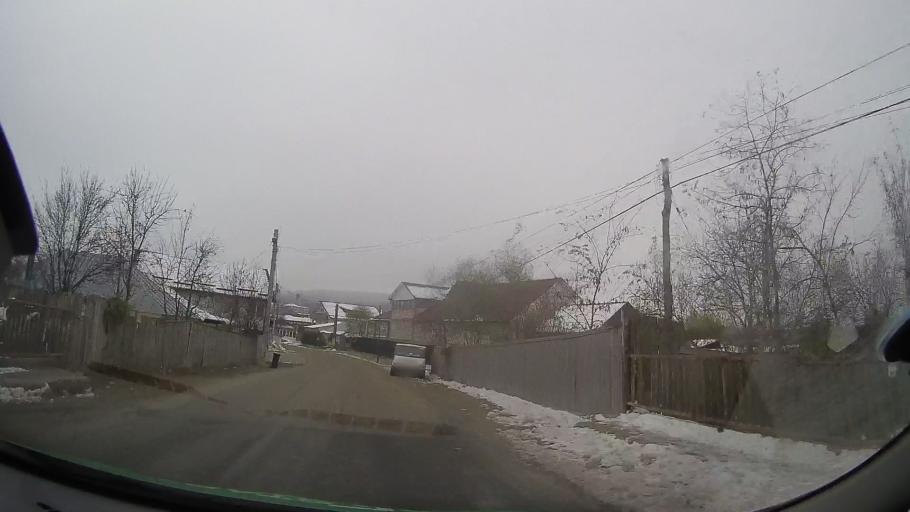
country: RO
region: Bacau
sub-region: Comuna Podu Turcului
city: Podu Turcului
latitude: 46.2055
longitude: 27.3818
